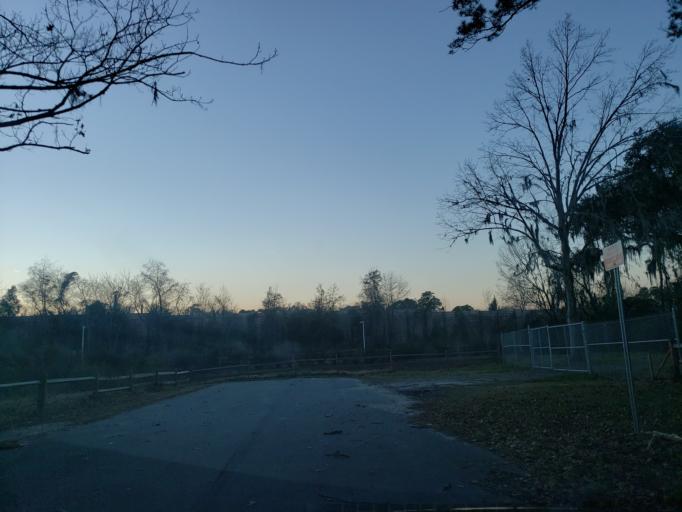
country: US
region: Georgia
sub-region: Chatham County
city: Thunderbolt
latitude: 32.0212
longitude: -81.0873
